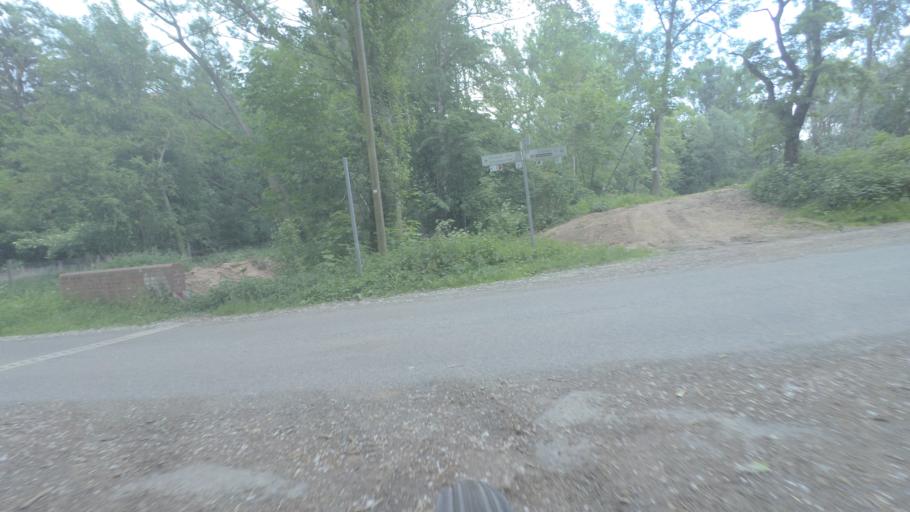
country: DE
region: Saxony-Anhalt
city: Hoym
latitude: 51.7130
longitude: 11.3461
